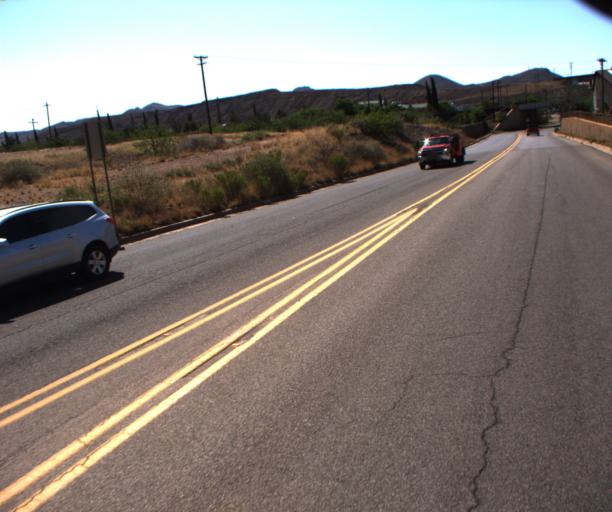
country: US
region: Arizona
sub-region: Cochise County
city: Bisbee
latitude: 31.4314
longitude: -109.8937
